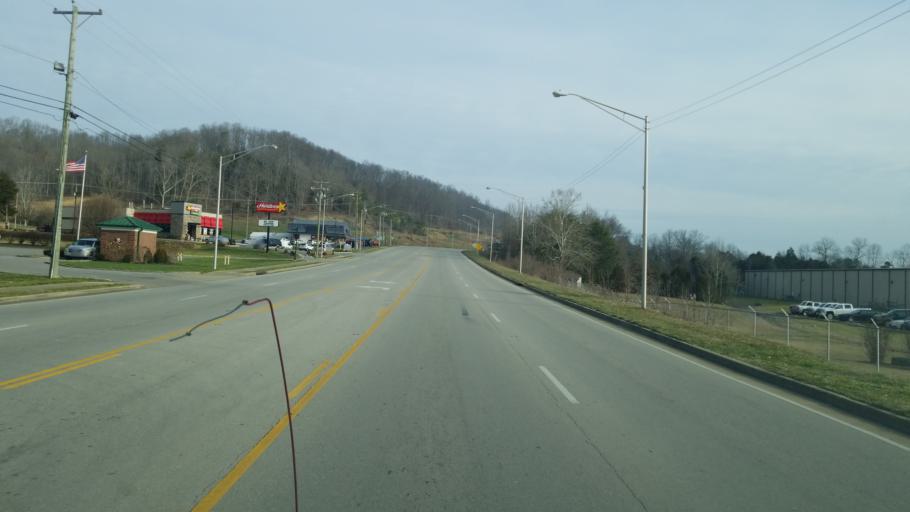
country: US
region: Kentucky
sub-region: Casey County
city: Liberty
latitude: 37.3236
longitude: -84.9246
